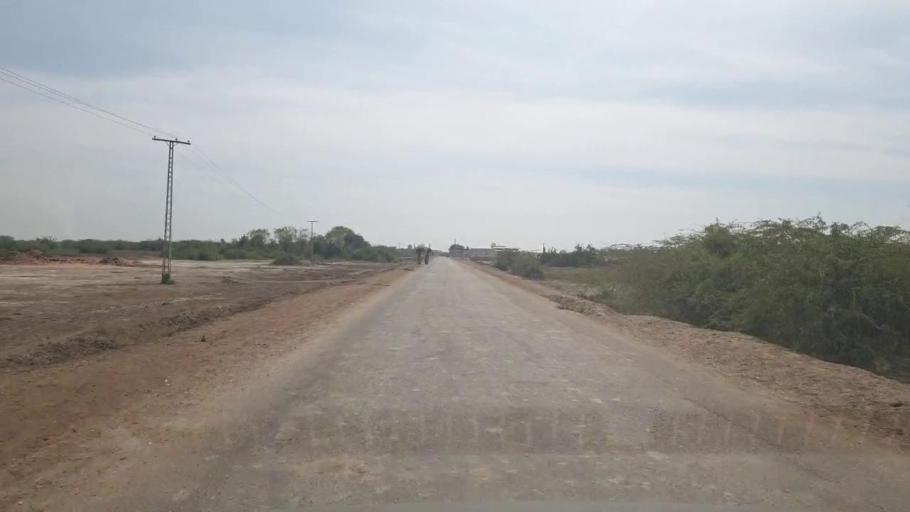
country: PK
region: Sindh
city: Umarkot
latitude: 25.3335
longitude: 69.5918
